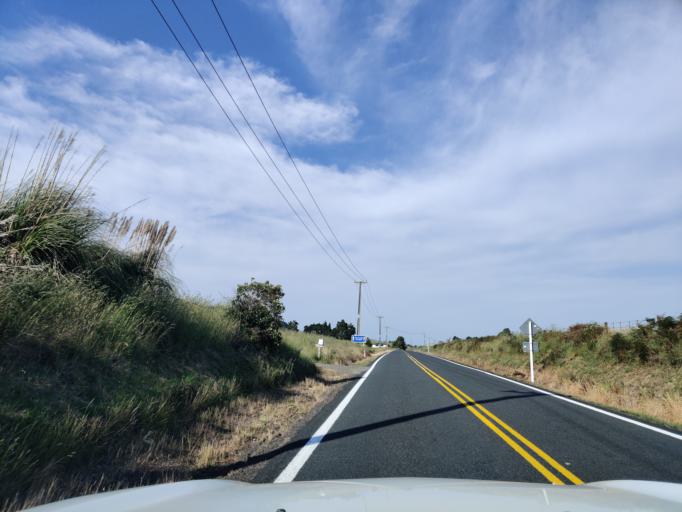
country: NZ
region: Waikato
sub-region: Waikato District
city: Ngaruawahia
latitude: -37.6302
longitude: 175.1627
